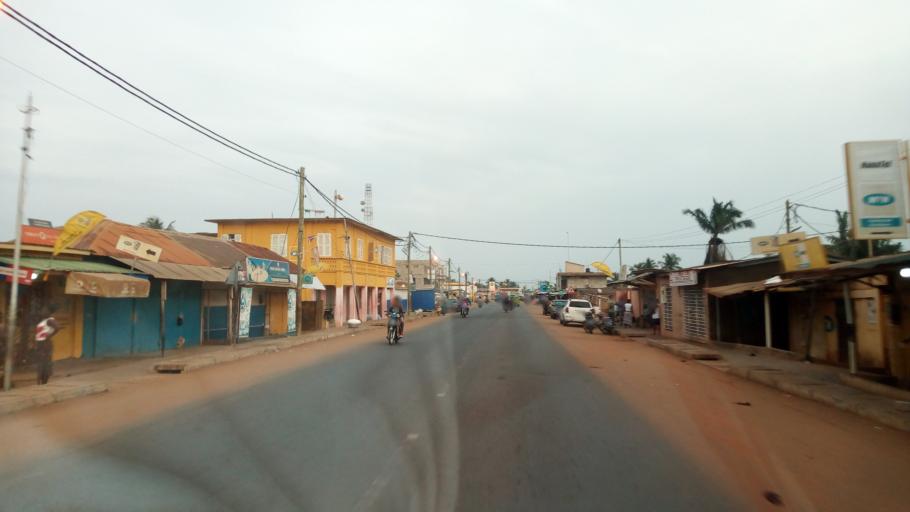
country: TG
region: Maritime
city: Lome
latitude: 6.1168
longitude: 1.1910
